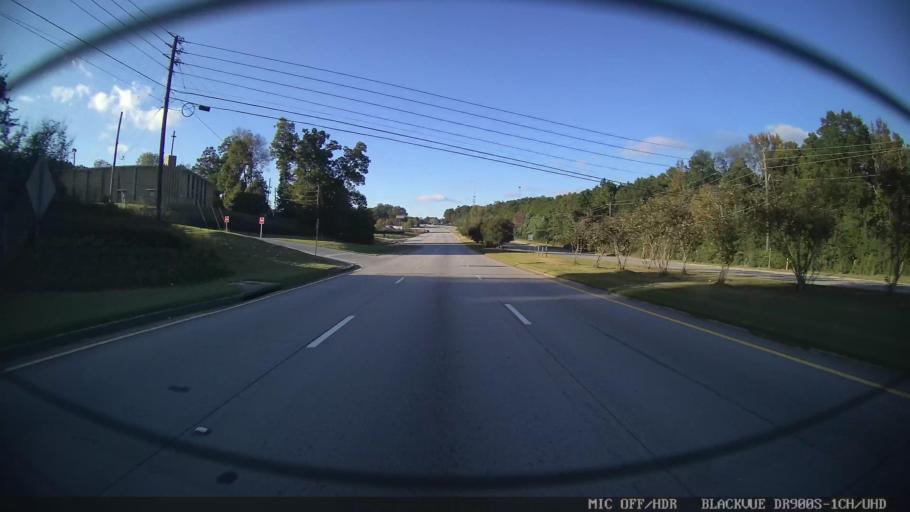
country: US
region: Georgia
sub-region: Clayton County
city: Conley
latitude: 33.6603
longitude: -84.3366
